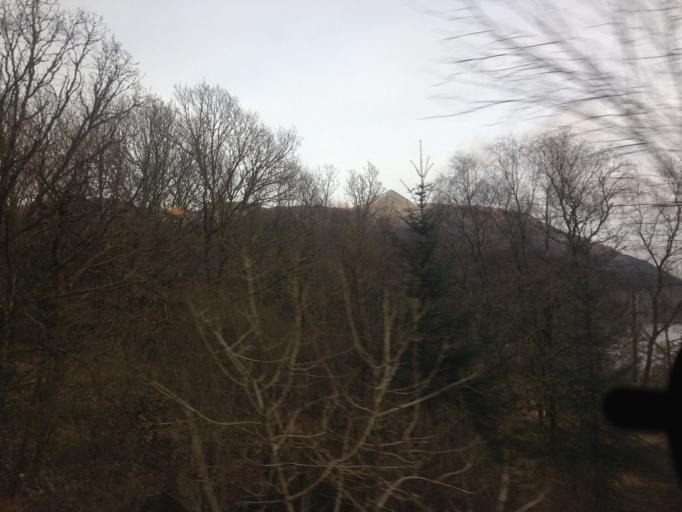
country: GB
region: Scotland
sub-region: Argyll and Bute
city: Garelochhead
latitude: 56.2072
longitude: -4.7103
